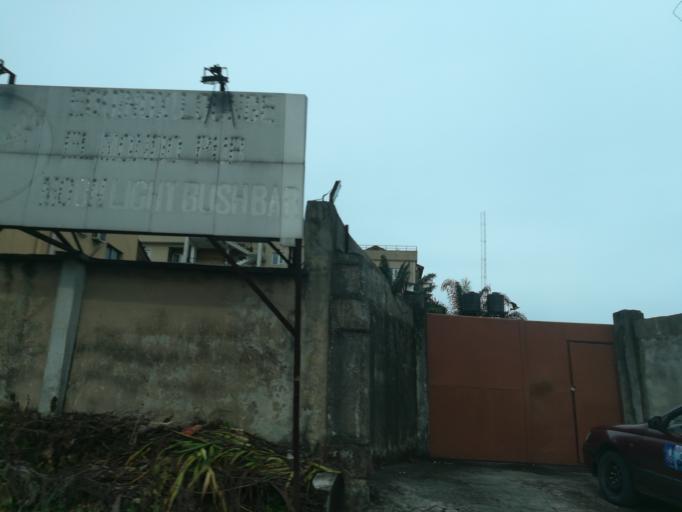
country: NG
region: Rivers
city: Port Harcourt
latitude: 4.8126
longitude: 6.9954
